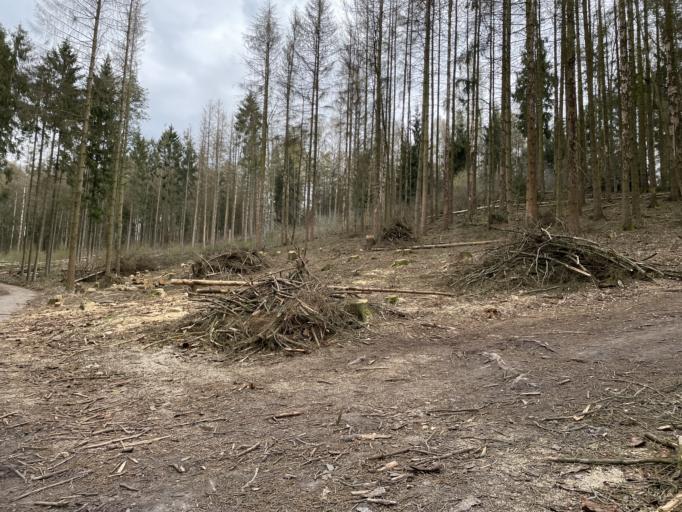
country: DE
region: North Rhine-Westphalia
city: Porta Westfalica
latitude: 52.2291
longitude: 8.9253
